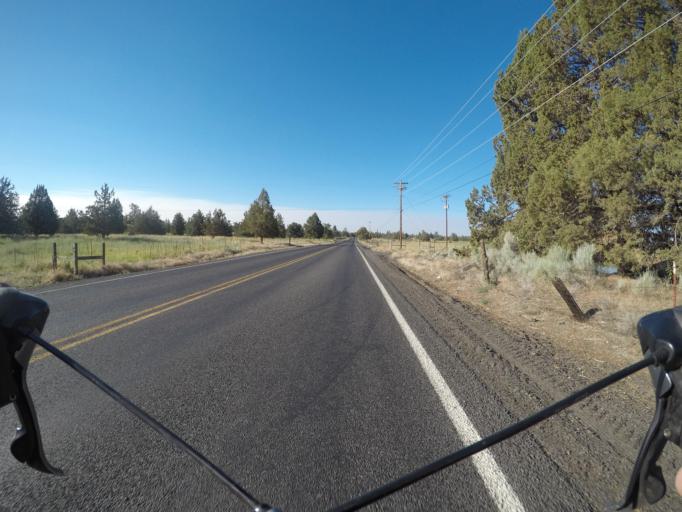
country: US
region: Oregon
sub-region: Deschutes County
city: Redmond
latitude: 44.2033
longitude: -121.2436
